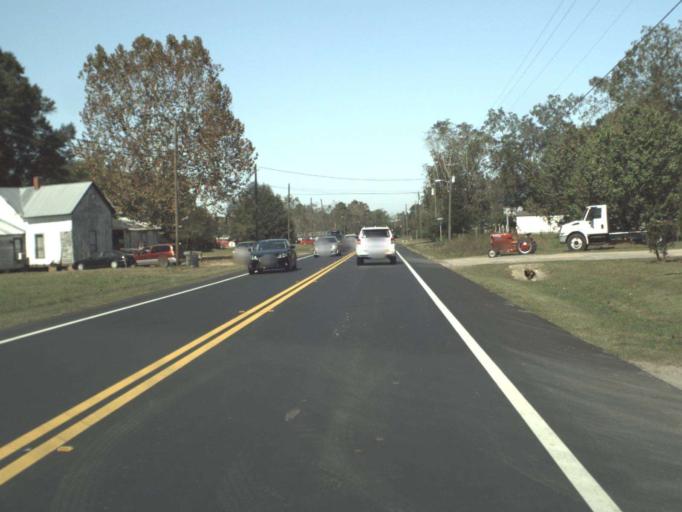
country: US
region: Alabama
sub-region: Covington County
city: Florala
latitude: 30.9781
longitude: -86.3052
